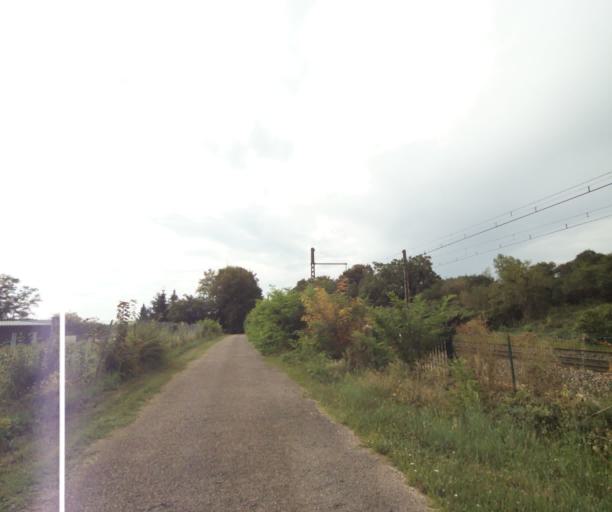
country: FR
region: Bourgogne
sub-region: Departement de Saone-et-Loire
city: Tournus
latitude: 46.5565
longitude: 4.9128
